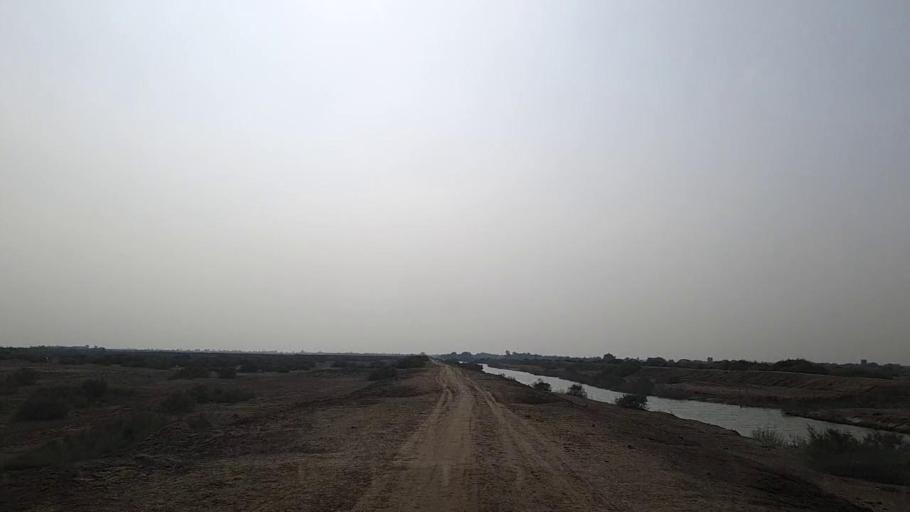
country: PK
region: Sindh
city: Gharo
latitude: 24.6691
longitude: 67.6381
